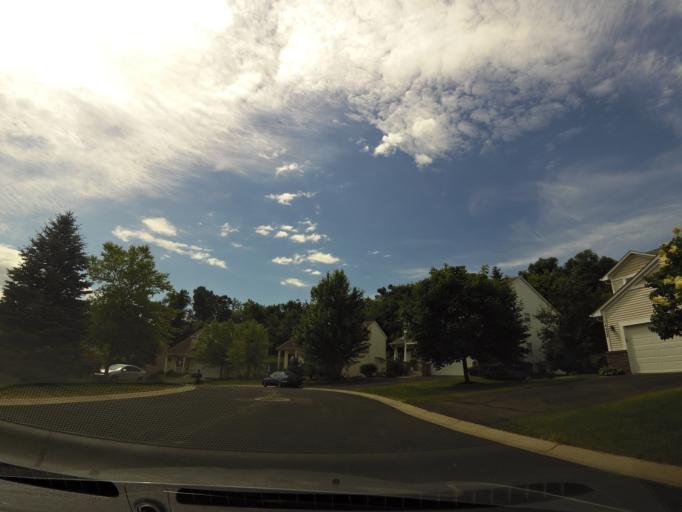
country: US
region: Minnesota
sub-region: Scott County
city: Prior Lake
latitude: 44.7402
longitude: -93.4741
